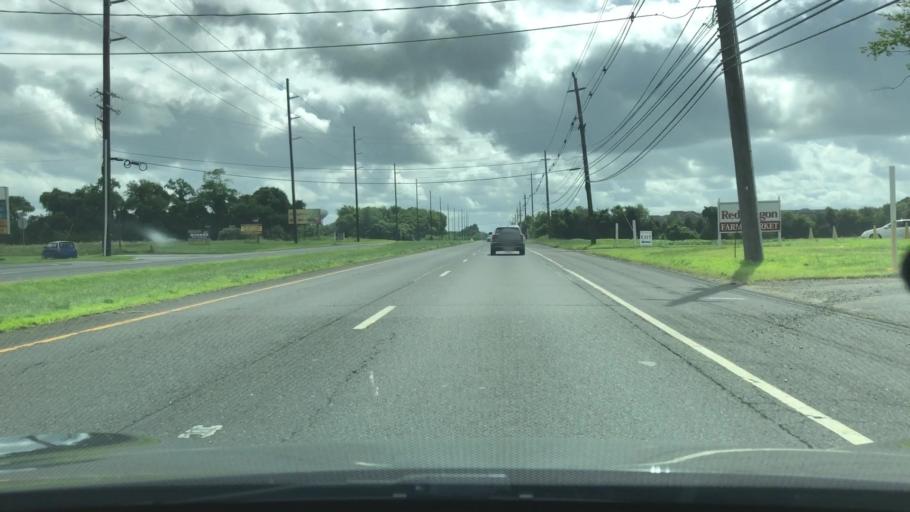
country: US
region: New Jersey
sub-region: Monmouth County
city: Englishtown
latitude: 40.2576
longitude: -74.3925
